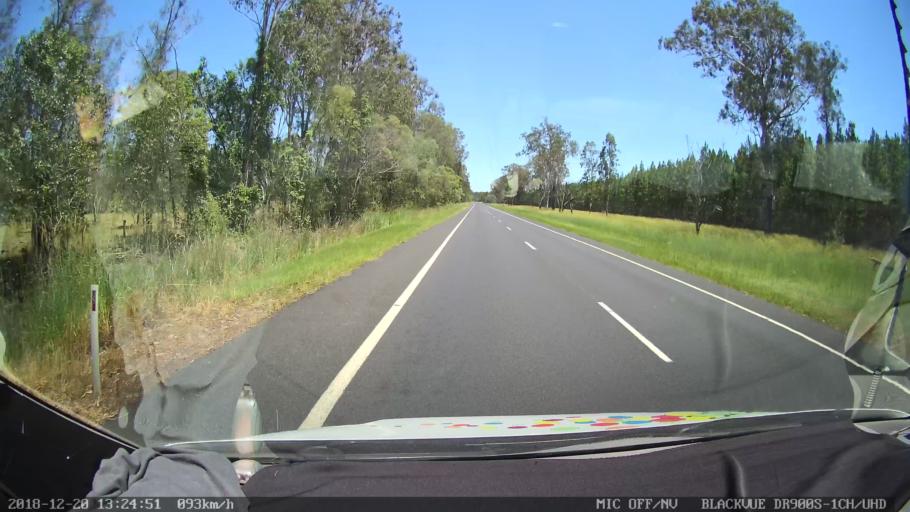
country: AU
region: New South Wales
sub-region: Richmond Valley
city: Casino
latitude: -29.1231
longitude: 152.9987
